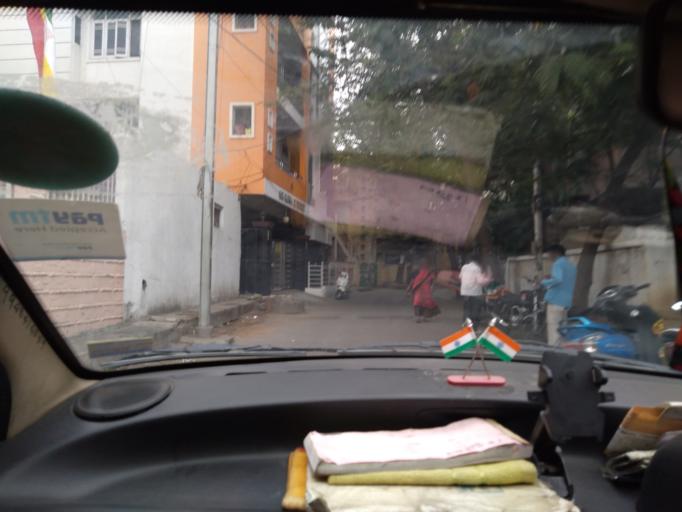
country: IN
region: Telangana
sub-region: Rangareddi
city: Gaddi Annaram
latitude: 17.3900
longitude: 78.4985
